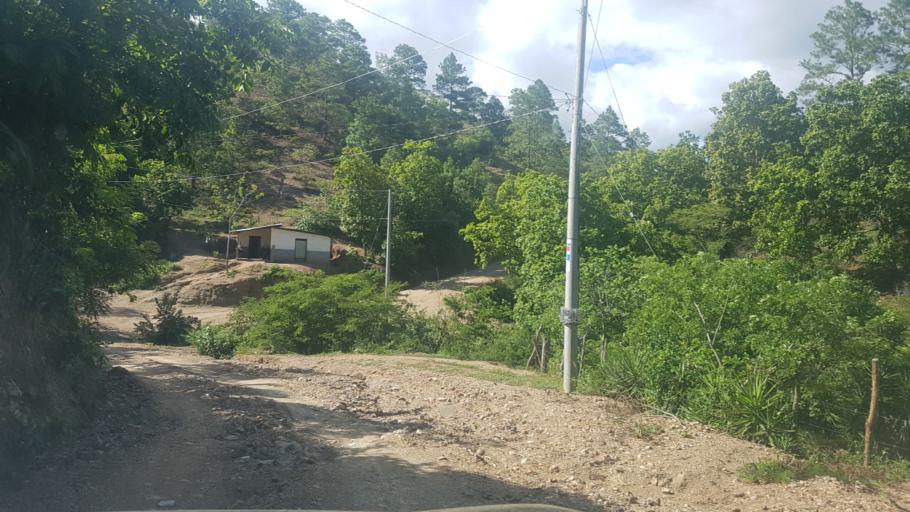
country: HN
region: Choluteca
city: Duyure
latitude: 13.6482
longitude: -86.6561
